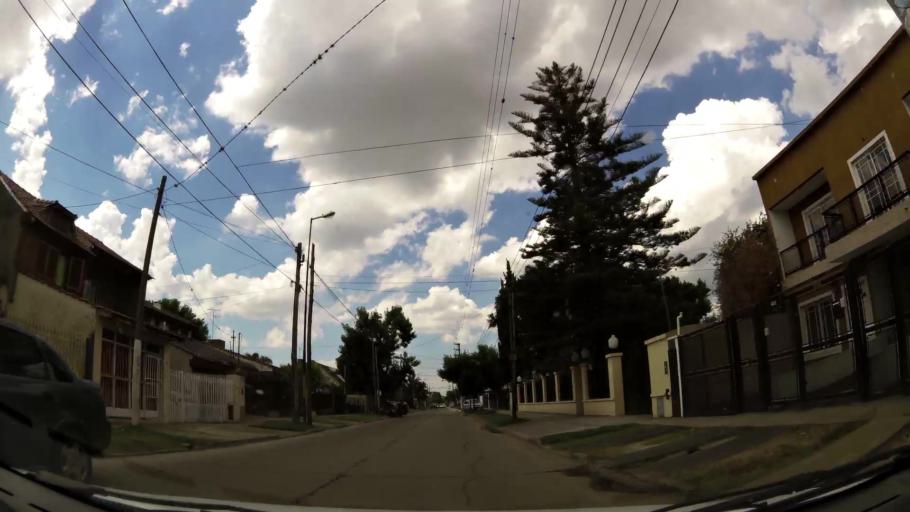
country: AR
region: Buenos Aires
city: Ituzaingo
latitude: -34.6439
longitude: -58.6777
